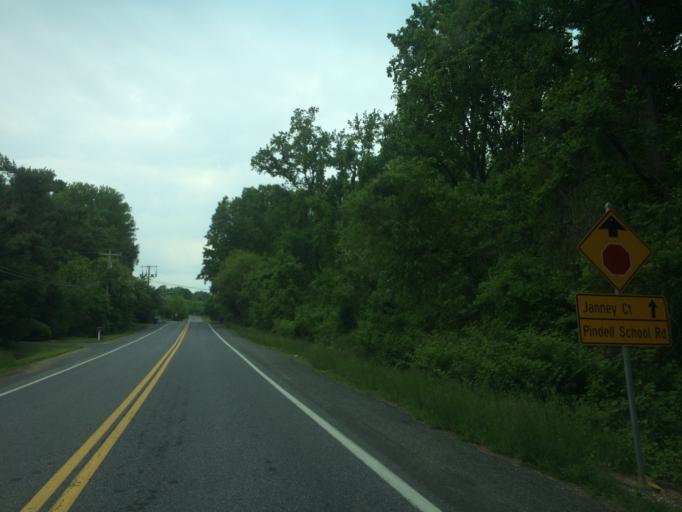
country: US
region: Maryland
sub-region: Howard County
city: Fulton
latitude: 39.1693
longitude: -76.9151
